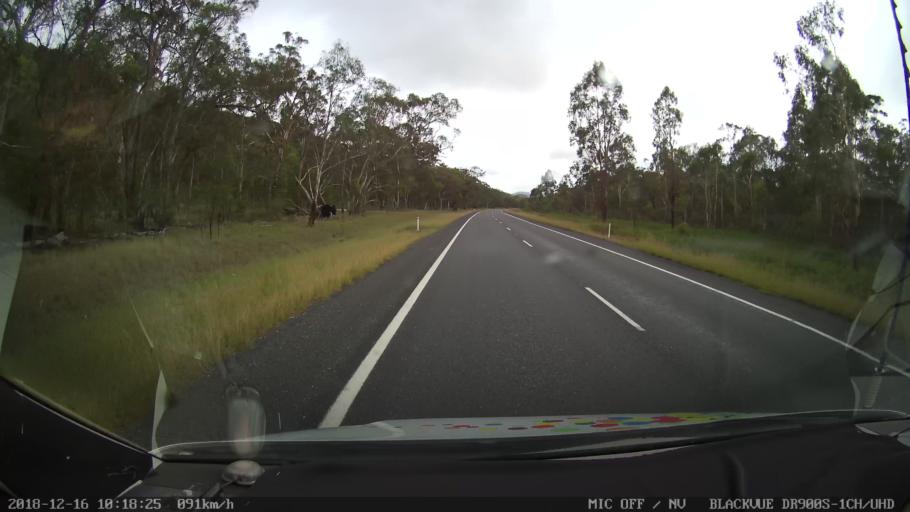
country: AU
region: New South Wales
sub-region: Tenterfield Municipality
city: Carrolls Creek
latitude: -29.2438
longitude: 151.9976
